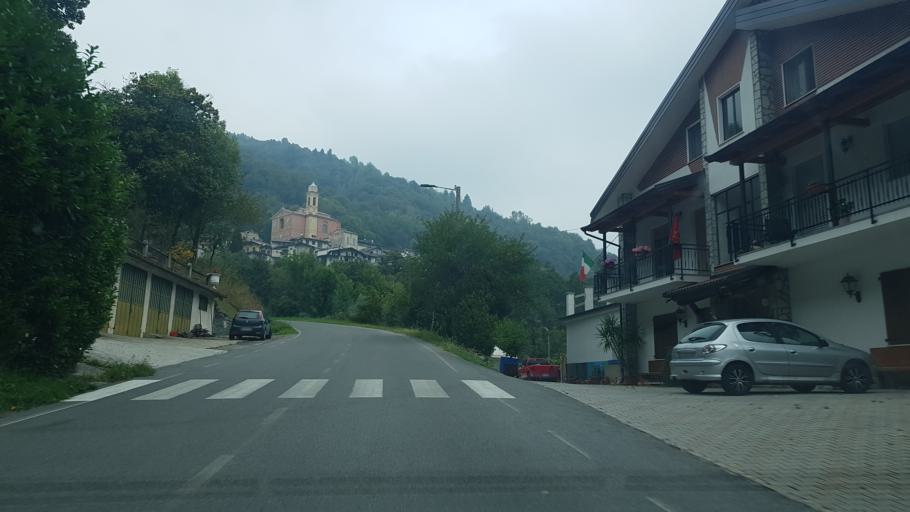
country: IT
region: Piedmont
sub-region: Provincia di Cuneo
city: Roccaforte Mondovi
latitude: 44.2759
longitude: 7.7383
